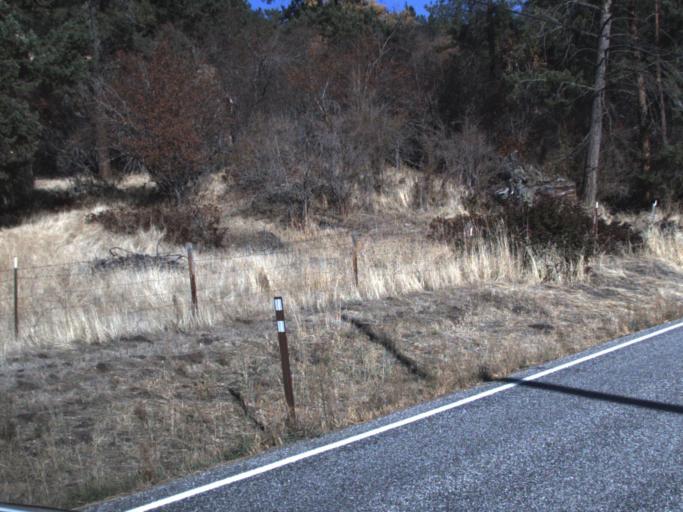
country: CA
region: British Columbia
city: Grand Forks
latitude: 48.9817
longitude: -118.5223
